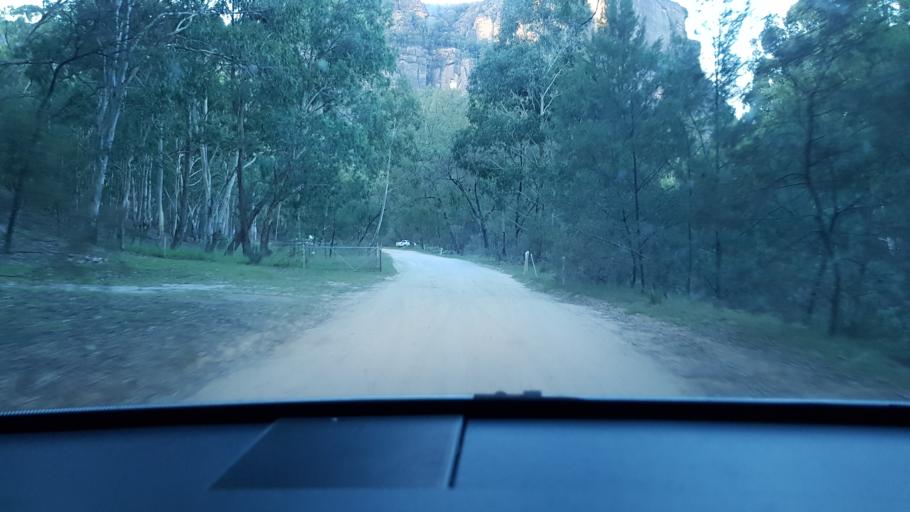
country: AU
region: New South Wales
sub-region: Lithgow
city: Portland
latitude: -33.1757
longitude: 150.2364
